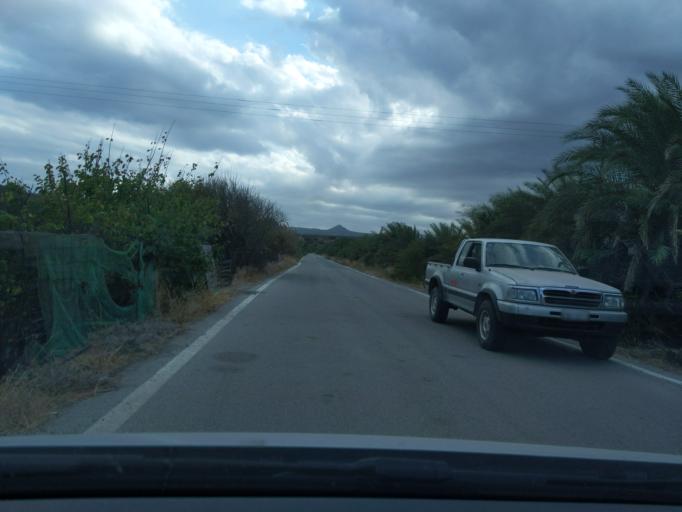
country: GR
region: Crete
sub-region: Nomos Lasithiou
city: Palekastro
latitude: 35.2579
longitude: 26.2551
